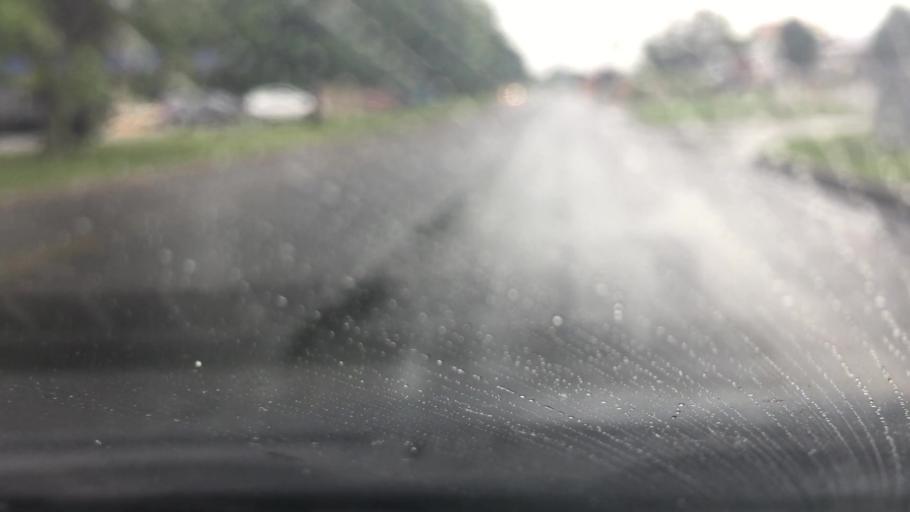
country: US
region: Illinois
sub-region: Williamson County
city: Marion
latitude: 37.7413
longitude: -88.9682
